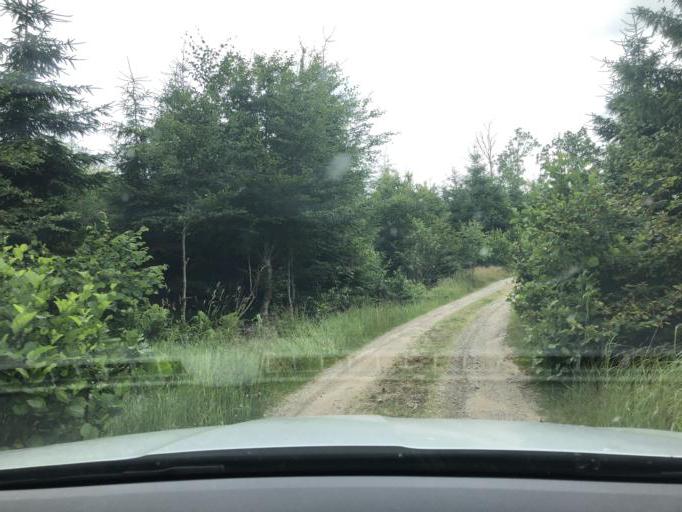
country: SE
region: Skane
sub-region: Bromolla Kommun
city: Nasum
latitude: 56.1559
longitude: 14.5743
